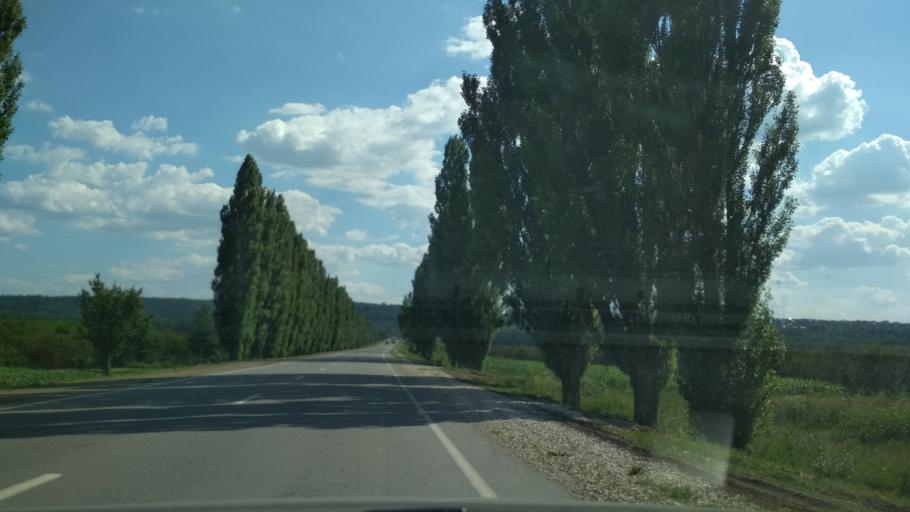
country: MD
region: Chisinau
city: Vadul lui Voda
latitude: 47.0989
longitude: 29.0972
